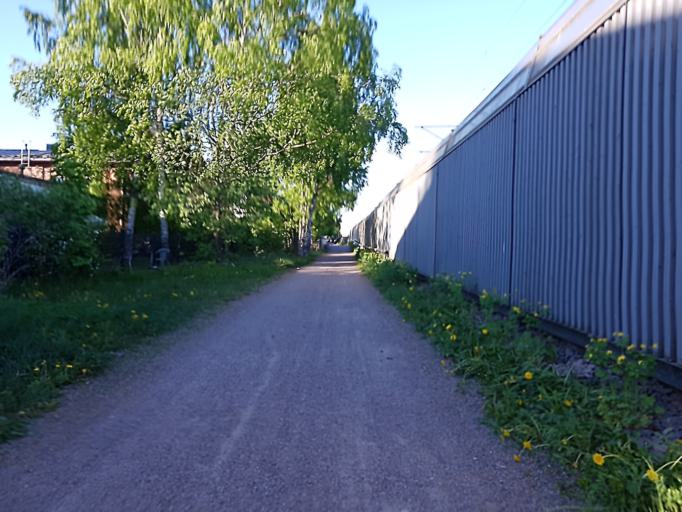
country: FI
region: Uusimaa
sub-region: Helsinki
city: Helsinki
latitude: 60.2267
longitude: 24.9628
